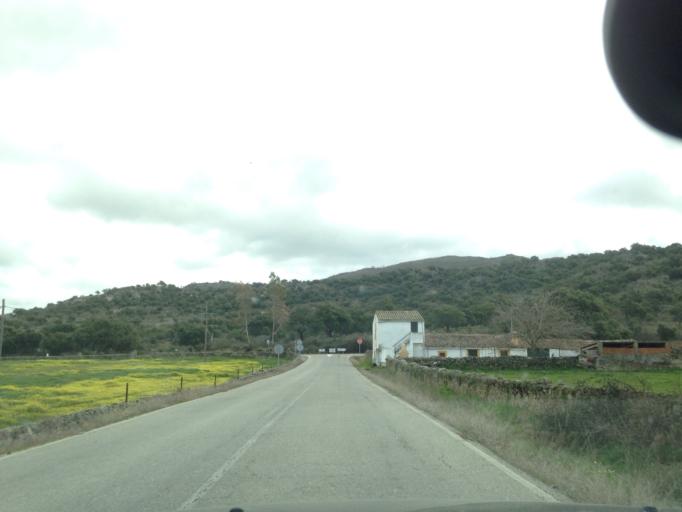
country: ES
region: Extremadura
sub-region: Provincia de Caceres
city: Montanchez
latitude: 39.2501
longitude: -6.1527
